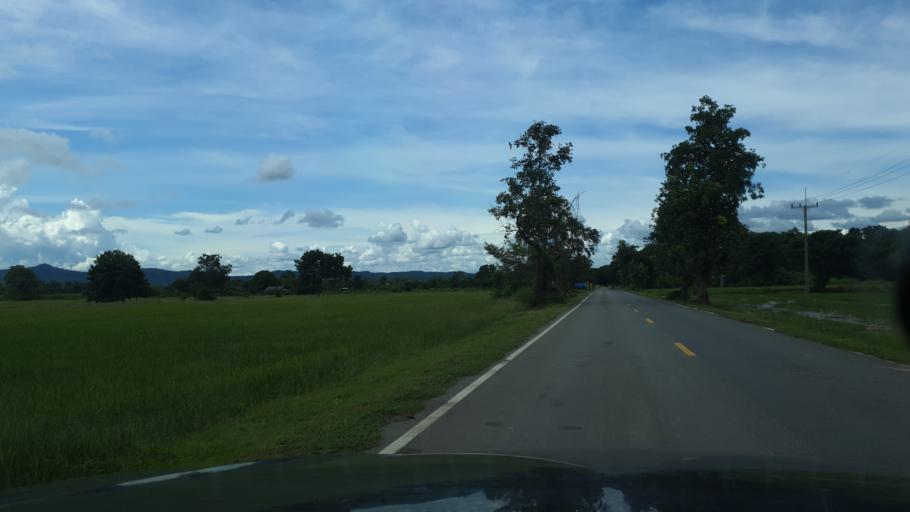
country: TH
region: Sukhothai
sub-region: Amphoe Si Satchanalai
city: Si Satchanalai
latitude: 17.4719
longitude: 99.7547
